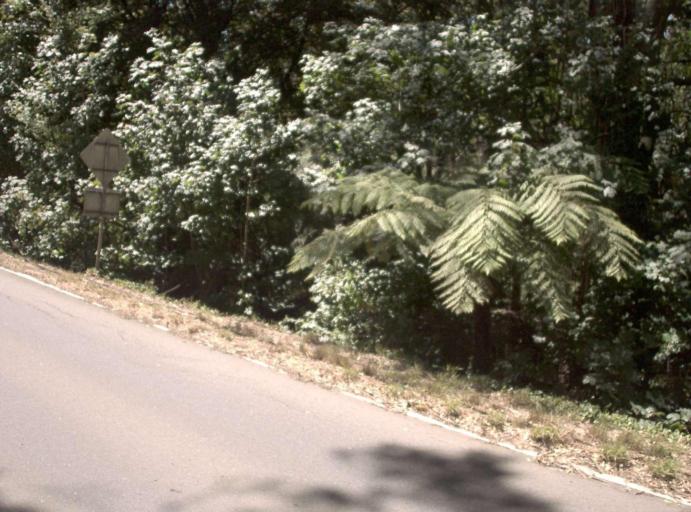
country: AU
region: Victoria
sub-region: Yarra Ranges
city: Ferny Creek
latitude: -37.8861
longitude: 145.3399
